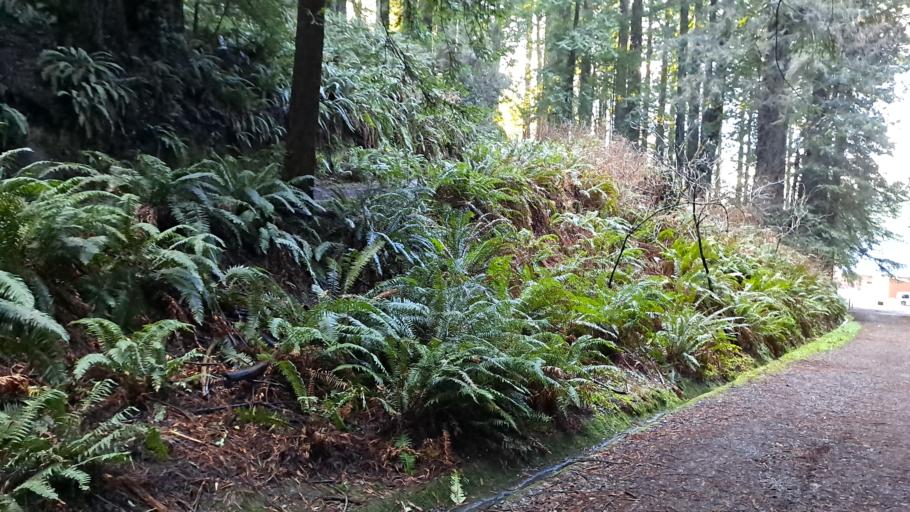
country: US
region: California
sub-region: Humboldt County
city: Fortuna
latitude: 40.6001
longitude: -124.1470
